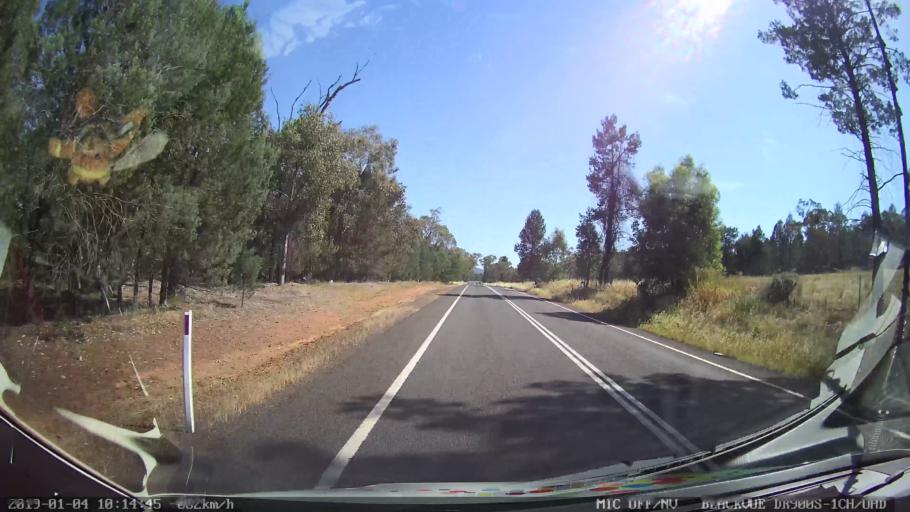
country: AU
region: New South Wales
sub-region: Cabonne
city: Canowindra
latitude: -33.3936
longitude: 148.4155
